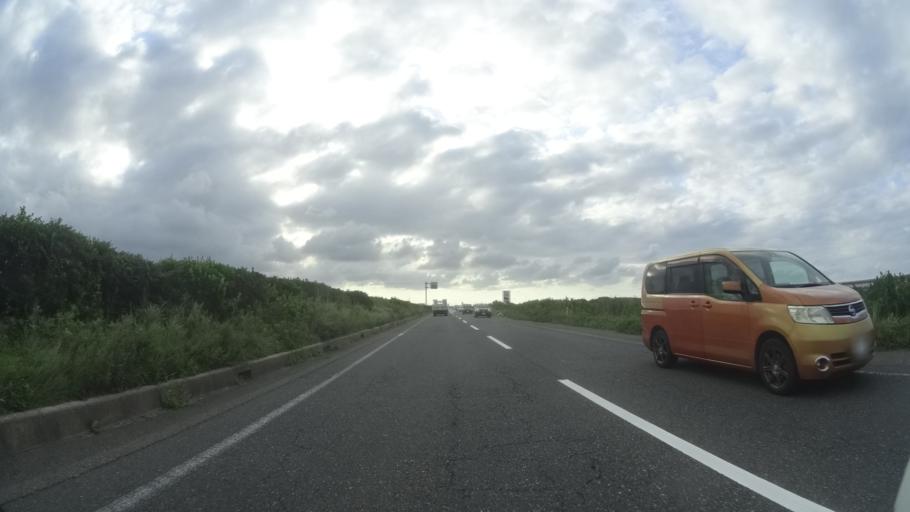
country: JP
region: Tottori
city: Kurayoshi
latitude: 35.5005
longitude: 133.7411
